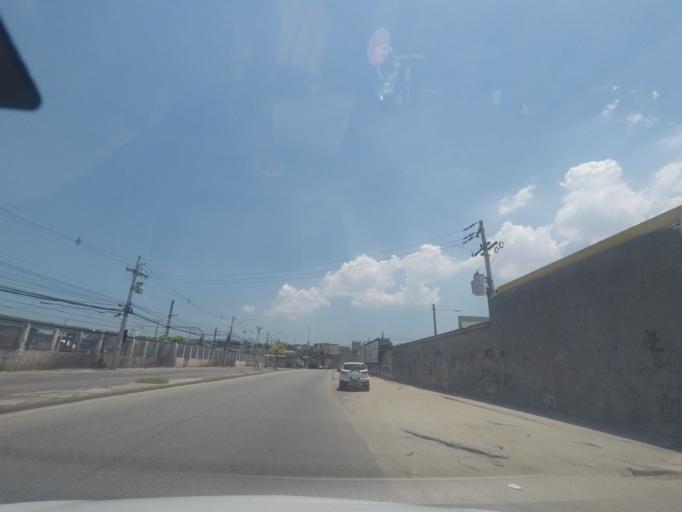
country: BR
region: Rio de Janeiro
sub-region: Duque De Caxias
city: Duque de Caxias
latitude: -22.8042
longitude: -43.3057
